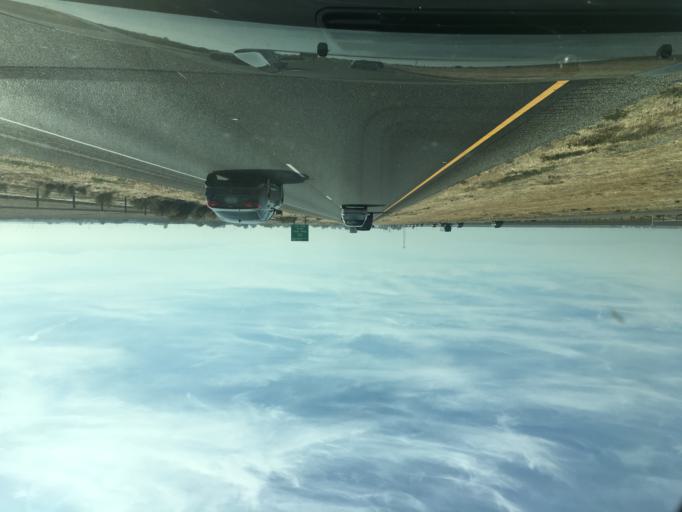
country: US
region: California
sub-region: Kern County
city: Rosedale
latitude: 35.2195
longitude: -119.1741
